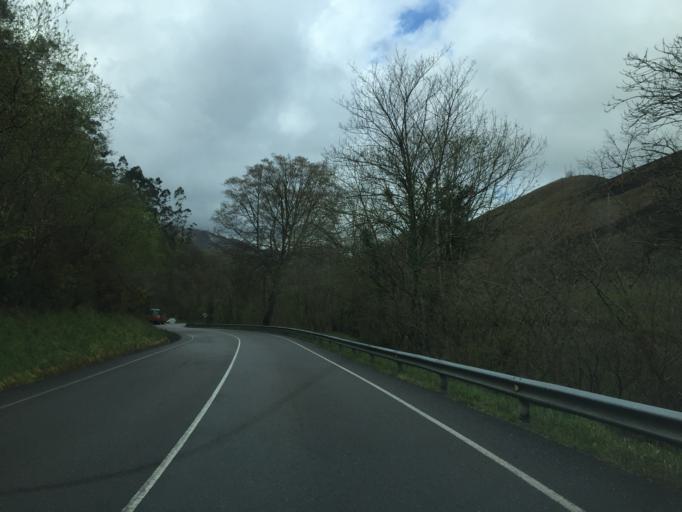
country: ES
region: Asturias
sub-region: Province of Asturias
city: Carrena
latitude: 43.3380
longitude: -4.9344
